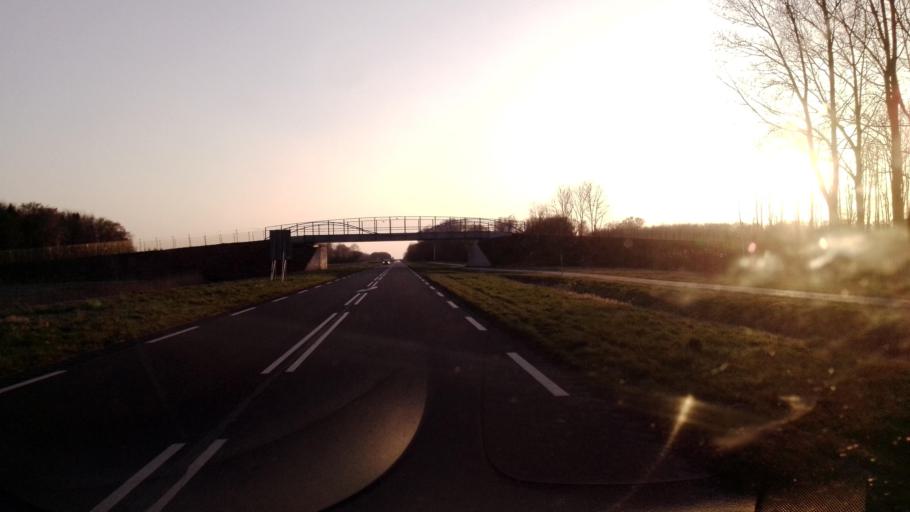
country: NL
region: Gelderland
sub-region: Gemeente Nunspeet
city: Nunspeet
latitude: 52.4334
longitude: 5.7592
